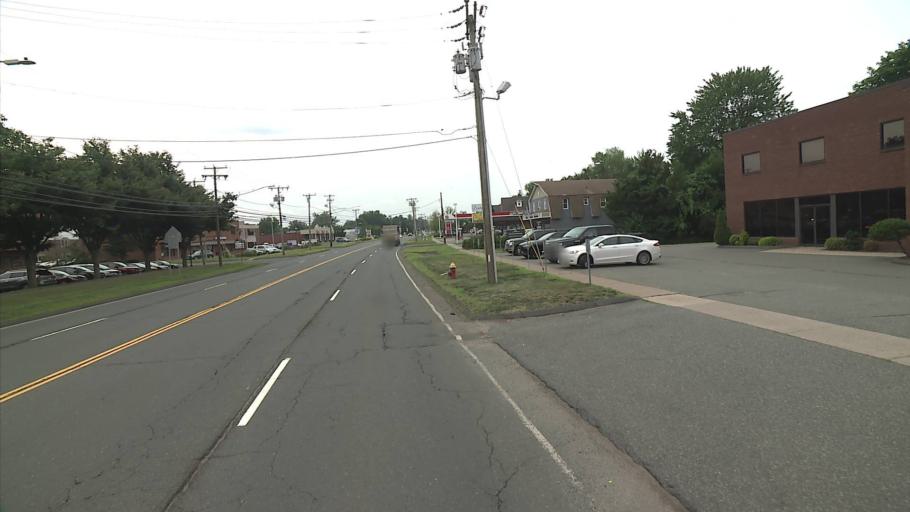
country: US
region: Connecticut
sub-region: Hartford County
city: Wethersfield
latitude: 41.6714
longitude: -72.6443
